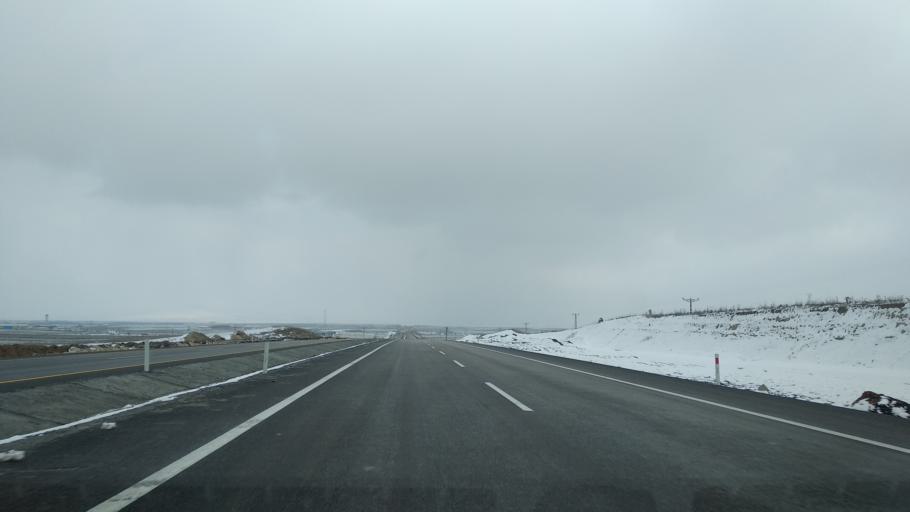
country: TR
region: Kayseri
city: Elbasi
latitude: 38.6534
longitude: 36.0076
